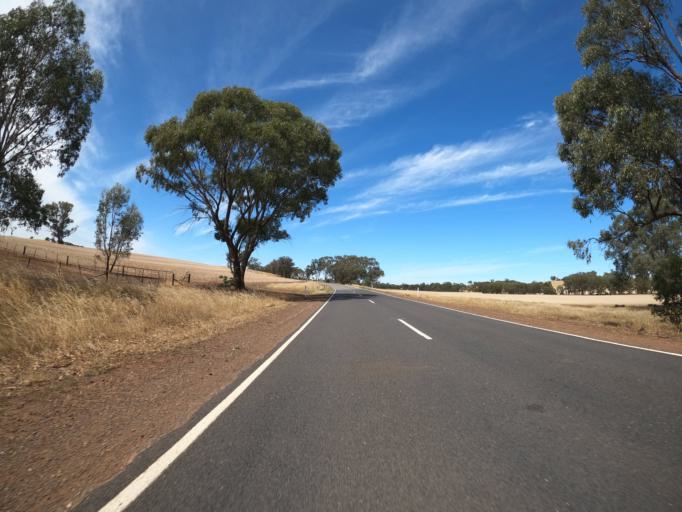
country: AU
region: Victoria
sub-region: Benalla
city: Benalla
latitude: -36.3343
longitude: 145.9597
